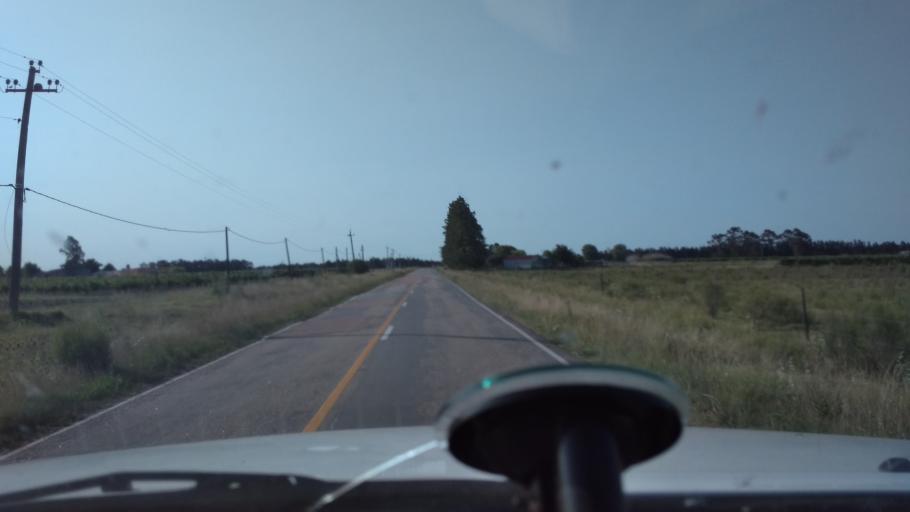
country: UY
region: Canelones
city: Sauce
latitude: -34.6115
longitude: -56.1238
